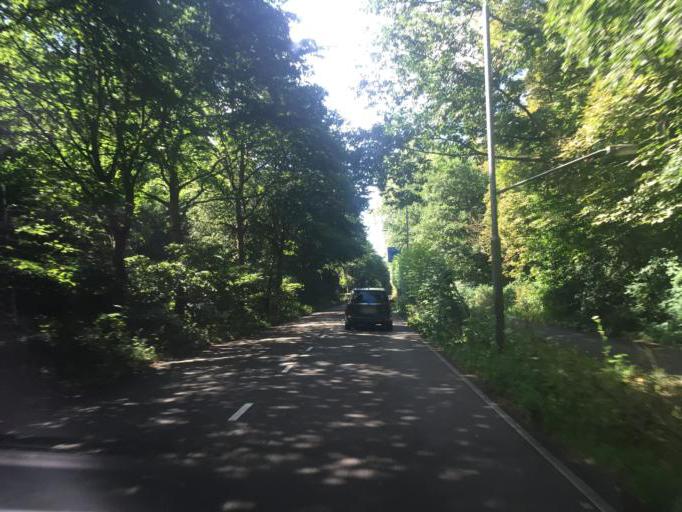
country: NL
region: North Holland
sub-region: Gemeente Haarlem
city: Haarlem
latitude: 52.3677
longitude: 4.6283
